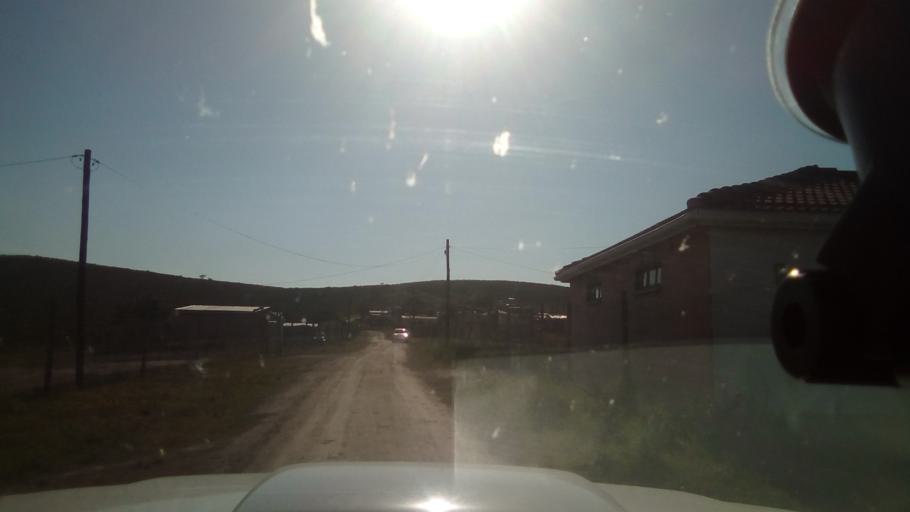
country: ZA
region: Eastern Cape
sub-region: Buffalo City Metropolitan Municipality
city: Bhisho
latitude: -32.8204
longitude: 27.3533
